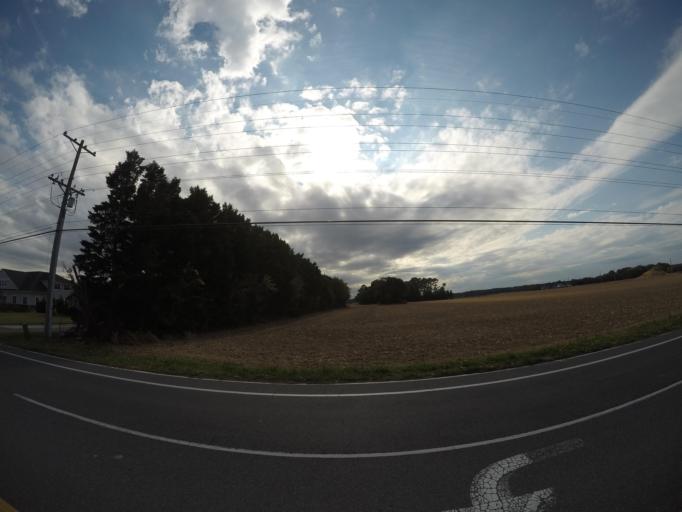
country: US
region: Delaware
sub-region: Sussex County
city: Lewes
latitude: 38.7289
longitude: -75.1481
